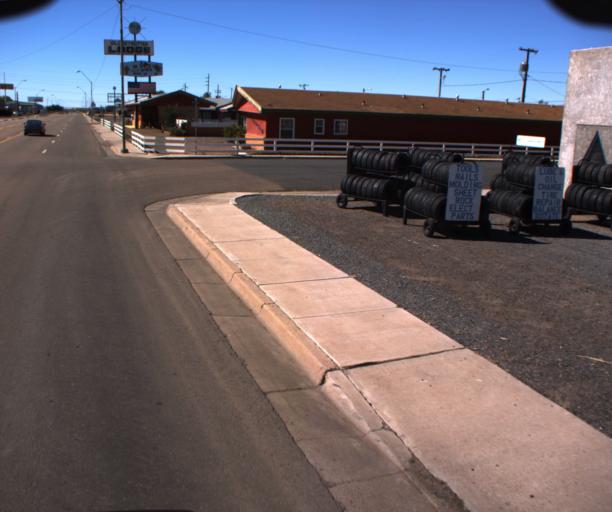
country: US
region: Arizona
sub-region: Navajo County
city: Holbrook
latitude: 34.9030
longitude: -110.1692
